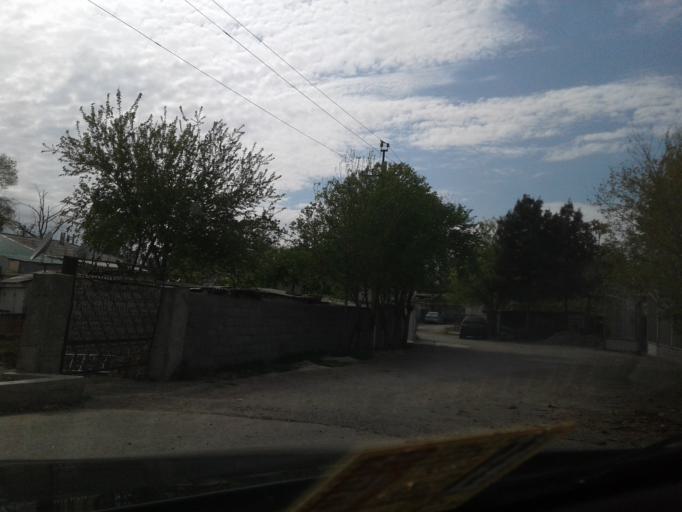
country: TM
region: Ahal
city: Ashgabat
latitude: 37.9782
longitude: 58.2958
